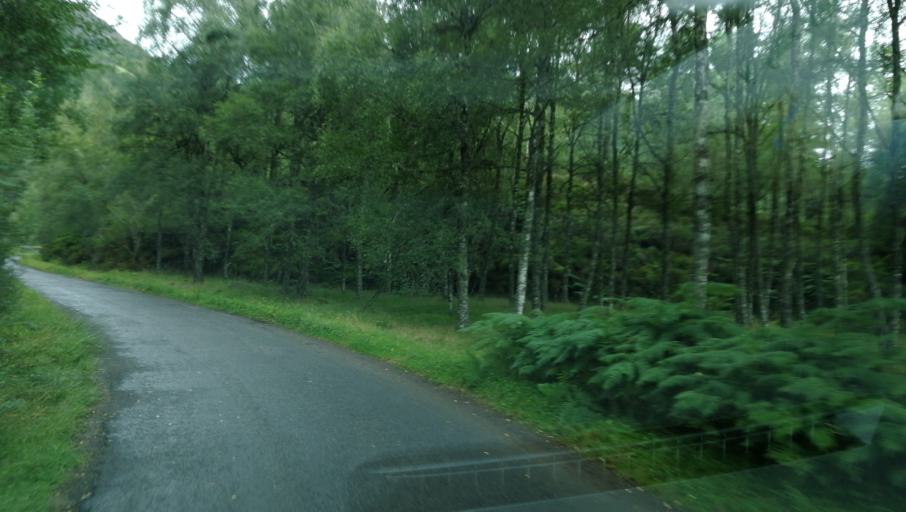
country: GB
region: Scotland
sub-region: Highland
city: Spean Bridge
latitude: 57.3040
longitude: -4.8740
